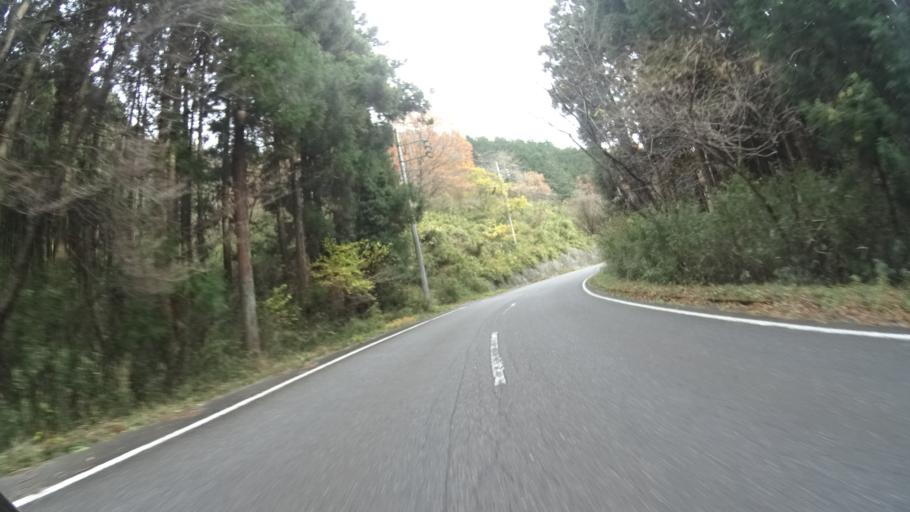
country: JP
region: Gunma
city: Omamacho-omama
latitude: 36.4787
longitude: 139.1656
